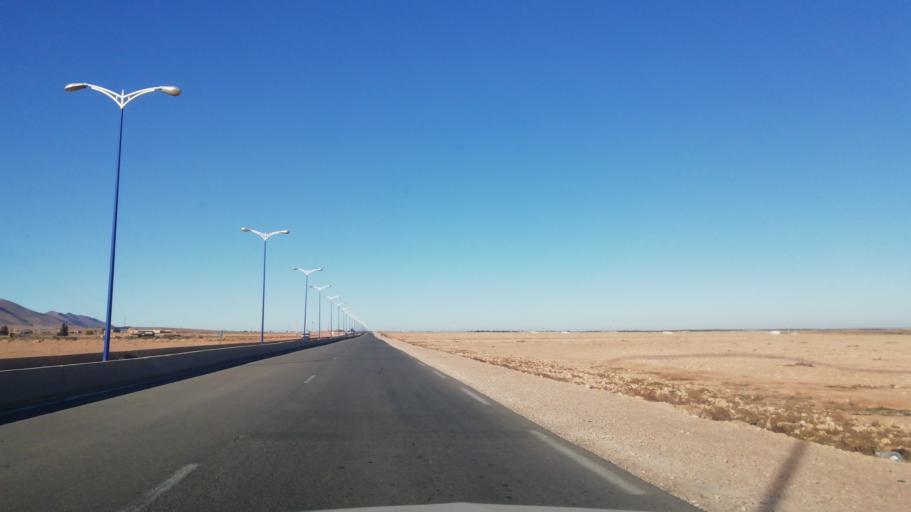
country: DZ
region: Wilaya de Naama
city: Naama
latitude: 33.5715
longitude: -0.2405
